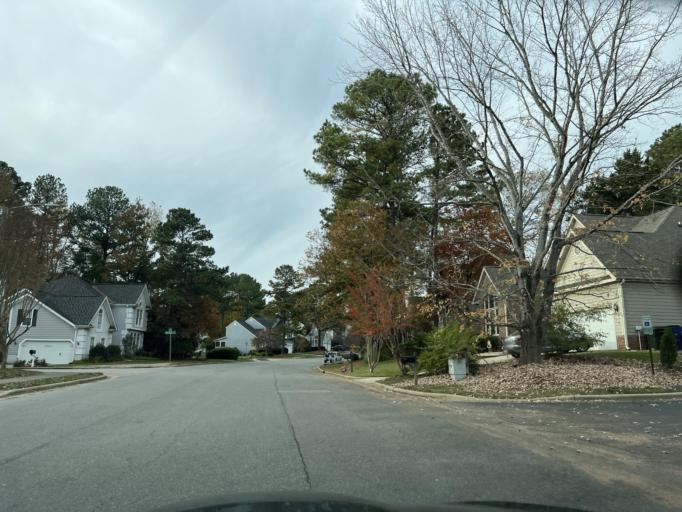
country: US
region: North Carolina
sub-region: Wake County
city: Wake Forest
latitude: 35.8930
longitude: -78.5940
